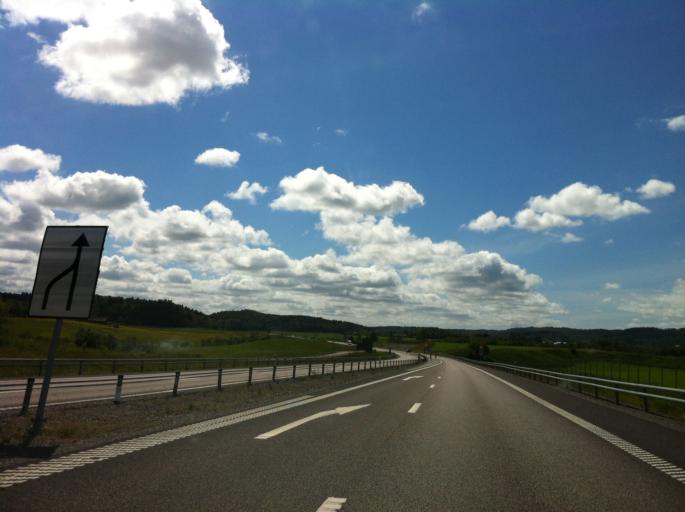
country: SE
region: Vaestra Goetaland
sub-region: Trollhattan
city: Sjuntorp
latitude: 58.2056
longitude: 12.1627
